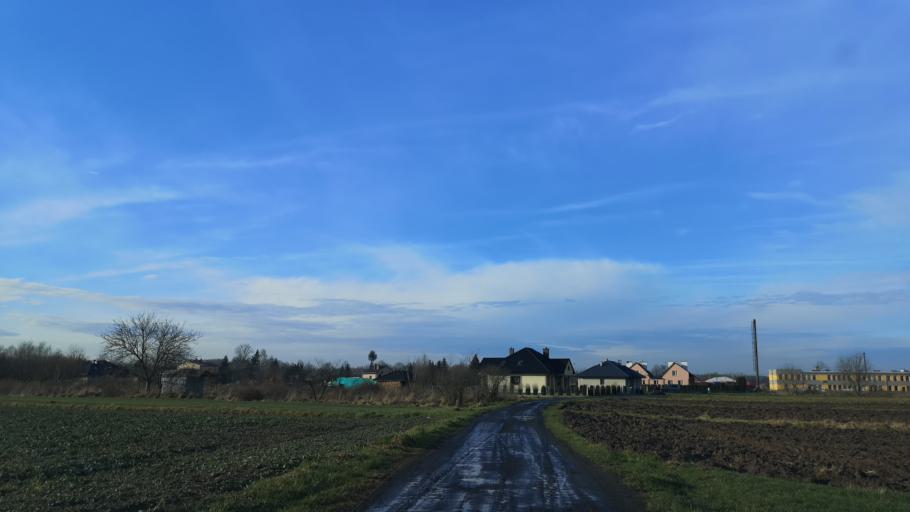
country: PL
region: Subcarpathian Voivodeship
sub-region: Powiat lezajski
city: Lezajsk
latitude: 50.2671
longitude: 22.4381
